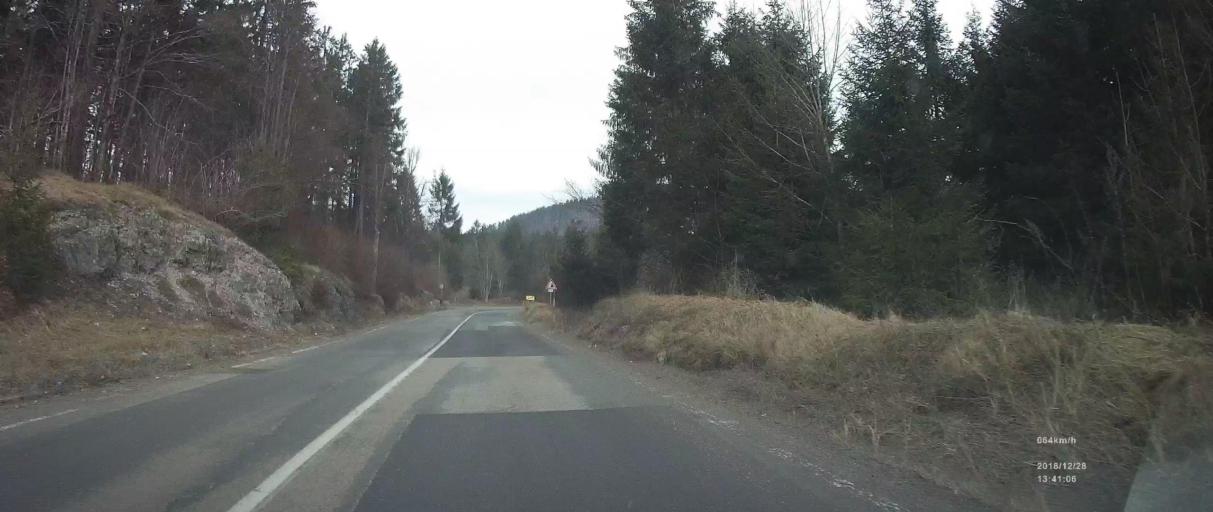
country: HR
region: Primorsko-Goranska
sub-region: Grad Delnice
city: Delnice
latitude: 45.3519
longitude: 14.7553
